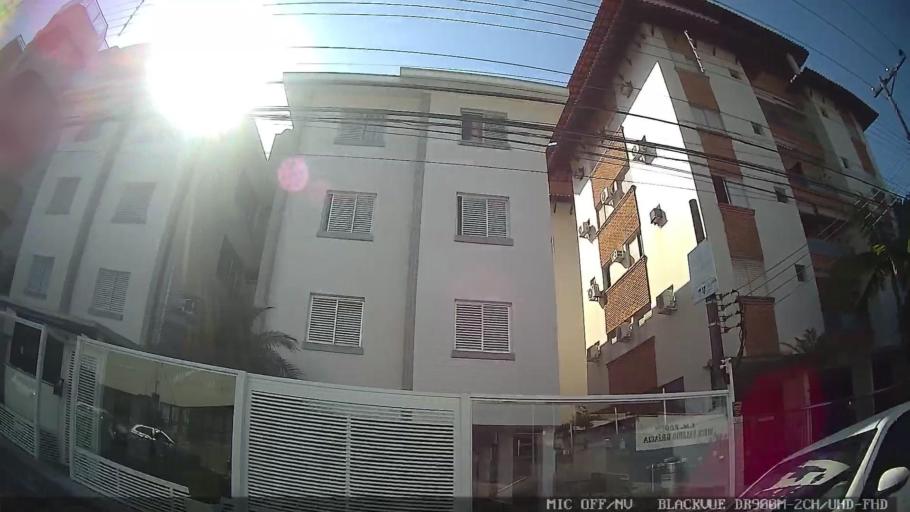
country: BR
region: Sao Paulo
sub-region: Guaruja
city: Guaruja
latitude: -23.9886
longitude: -46.2470
